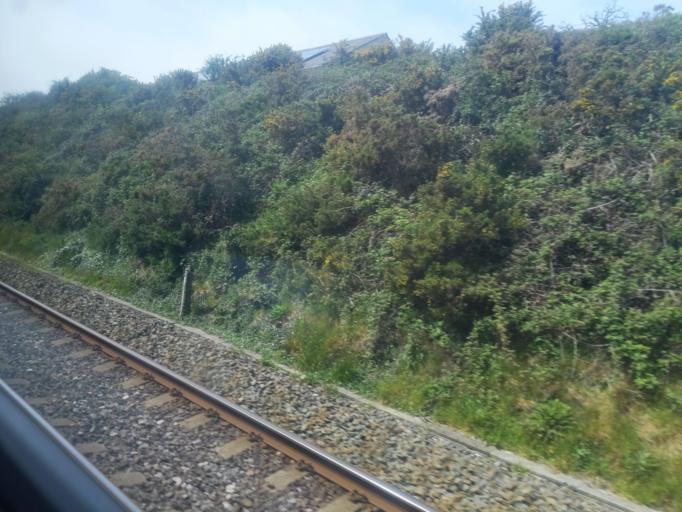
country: GB
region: England
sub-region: Cornwall
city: Redruth
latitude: 50.2268
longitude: -5.2485
